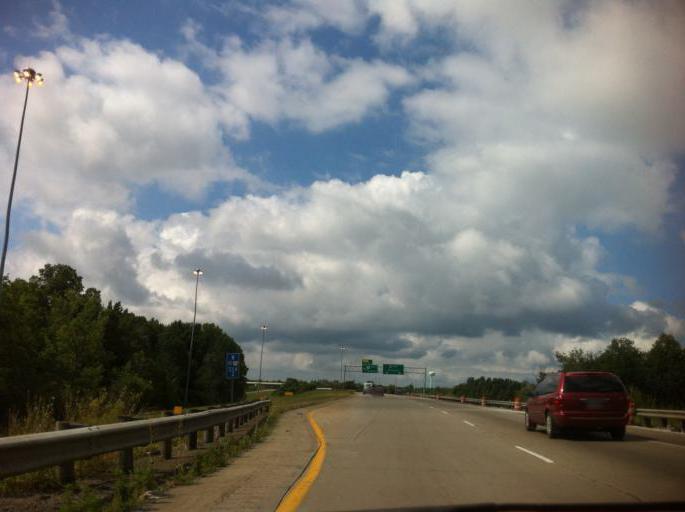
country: US
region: Ohio
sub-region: Trumbull County
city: Mineral Ridge
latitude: 41.1296
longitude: -80.7458
